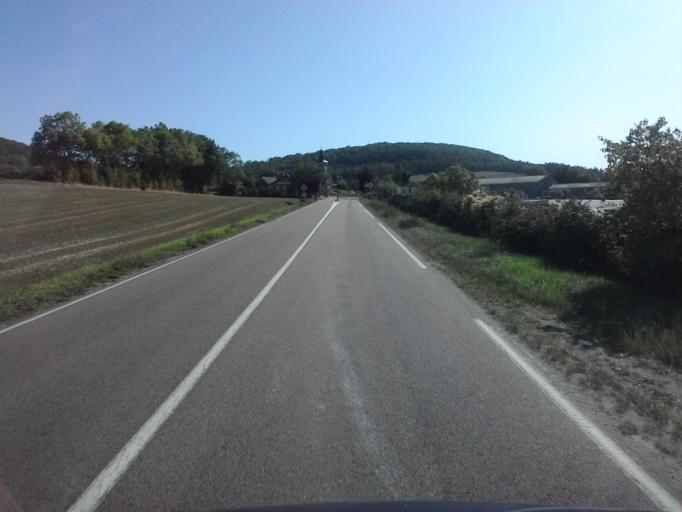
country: FR
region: Champagne-Ardenne
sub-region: Departement de l'Aube
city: Mussy-sur-Seine
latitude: 47.9312
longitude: 4.5377
